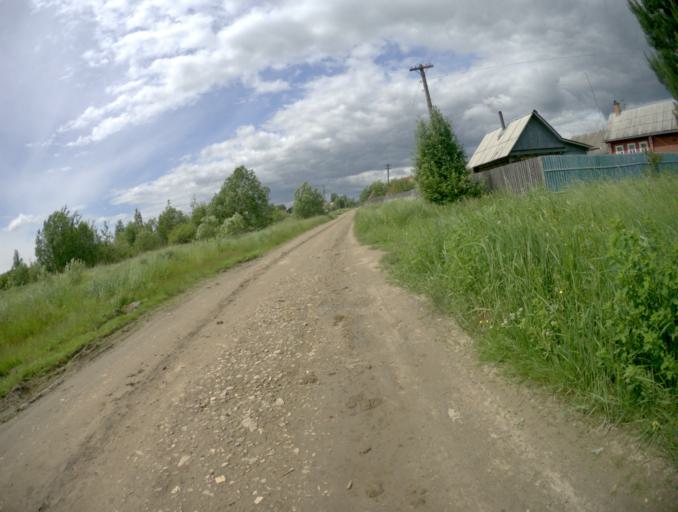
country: RU
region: Ivanovo
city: Savino
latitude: 56.5889
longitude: 41.2281
